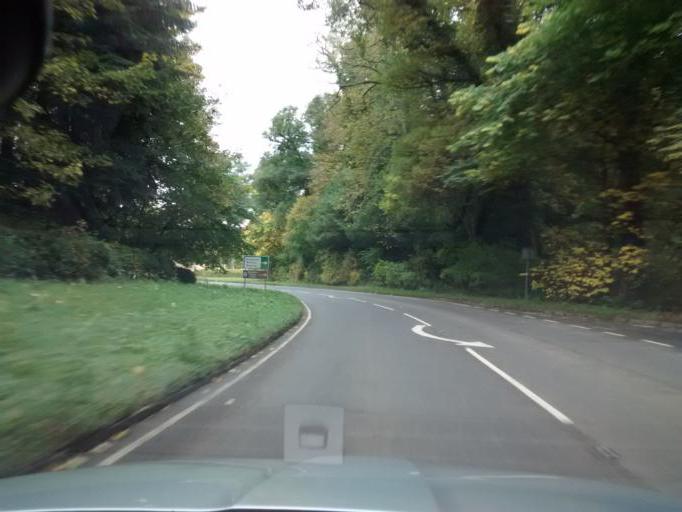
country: GB
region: Scotland
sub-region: Perth and Kinross
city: Blairgowrie
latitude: 56.5307
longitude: -3.3645
